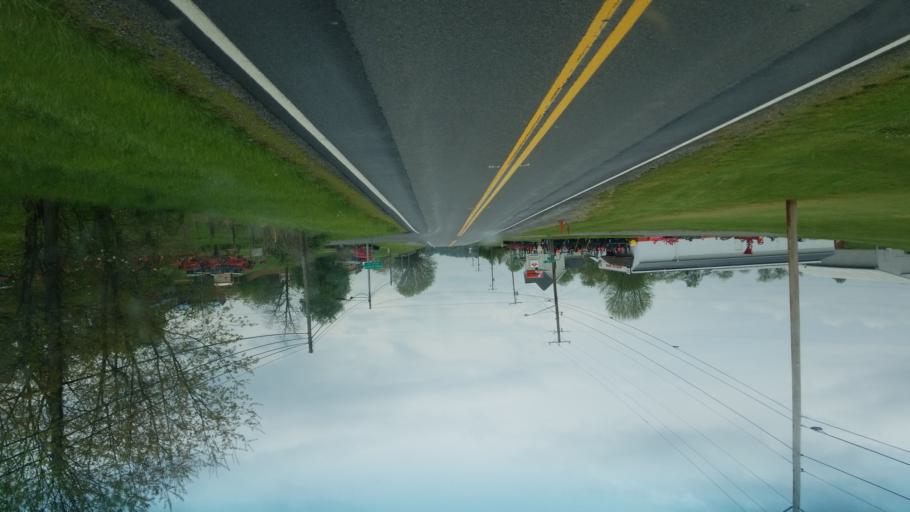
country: US
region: Virginia
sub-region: Wythe County
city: Rural Retreat
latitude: 36.9070
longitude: -81.2878
